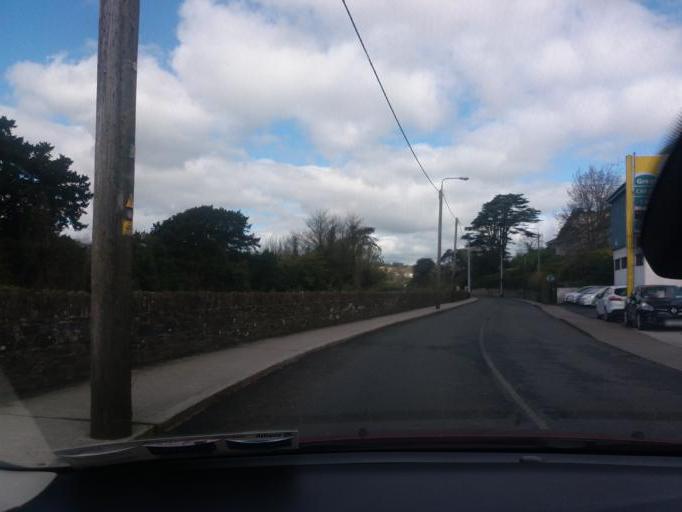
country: IE
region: Munster
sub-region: County Cork
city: Cobh
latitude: 51.8477
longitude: -8.3194
